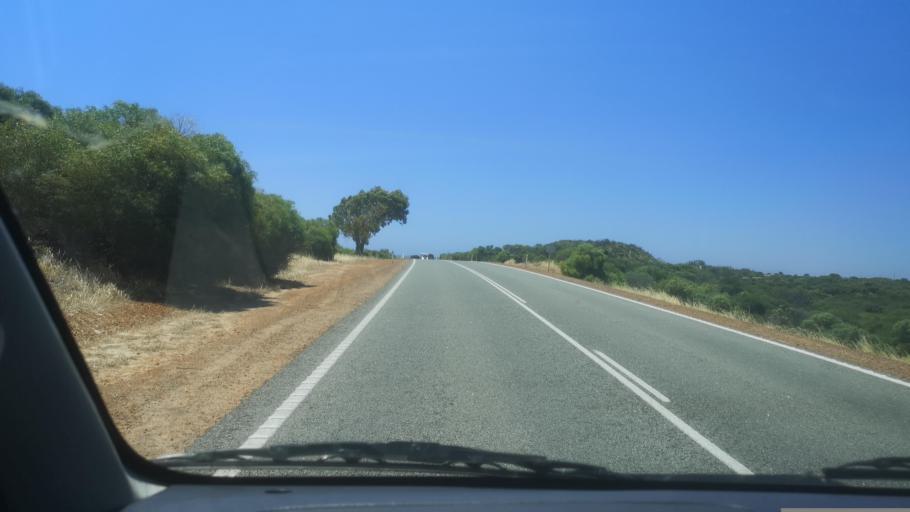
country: AU
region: Western Australia
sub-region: Dandaragan
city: Jurien Bay
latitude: -30.0174
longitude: 114.9722
